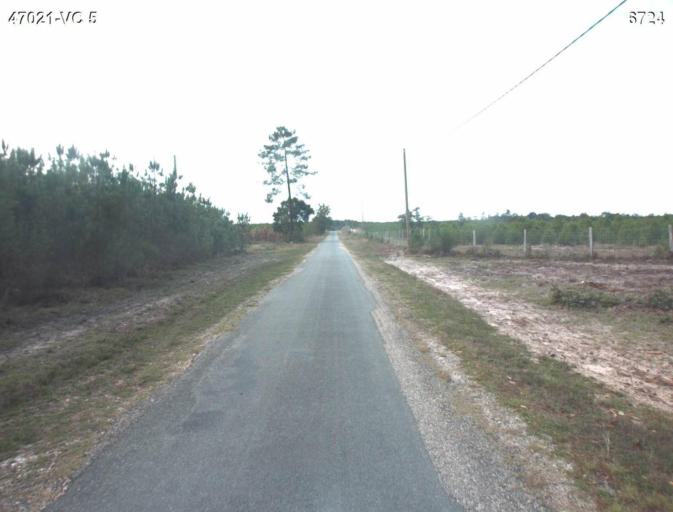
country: FR
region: Aquitaine
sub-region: Departement du Lot-et-Garonne
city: Barbaste
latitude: 44.1512
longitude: 0.2170
